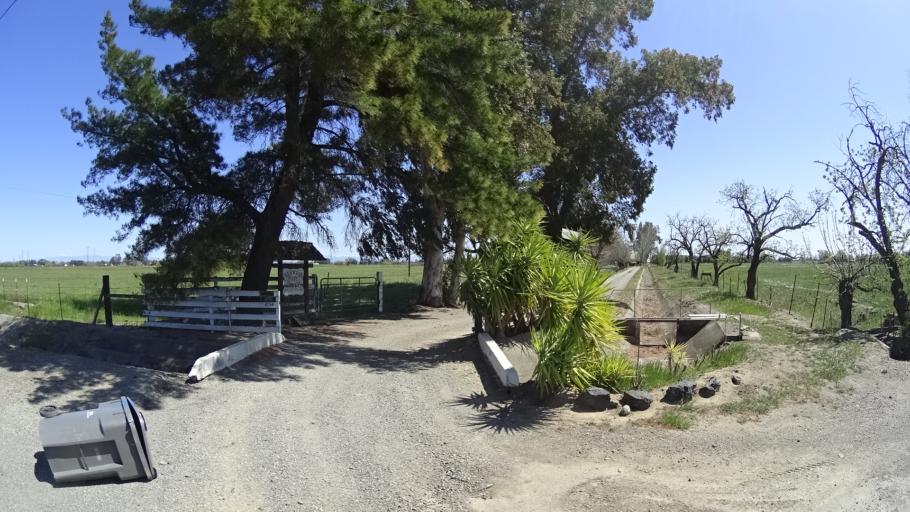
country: US
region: California
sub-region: Glenn County
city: Orland
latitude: 39.7769
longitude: -122.2712
